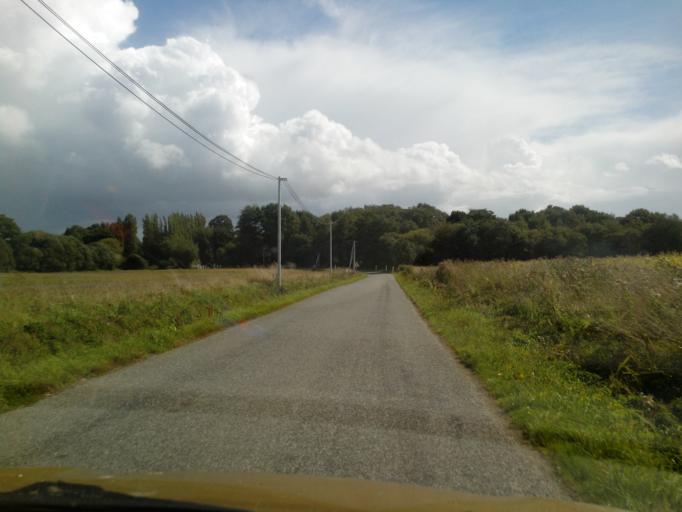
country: FR
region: Brittany
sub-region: Departement des Cotes-d'Armor
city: Merdrignac
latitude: 48.1559
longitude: -2.4172
